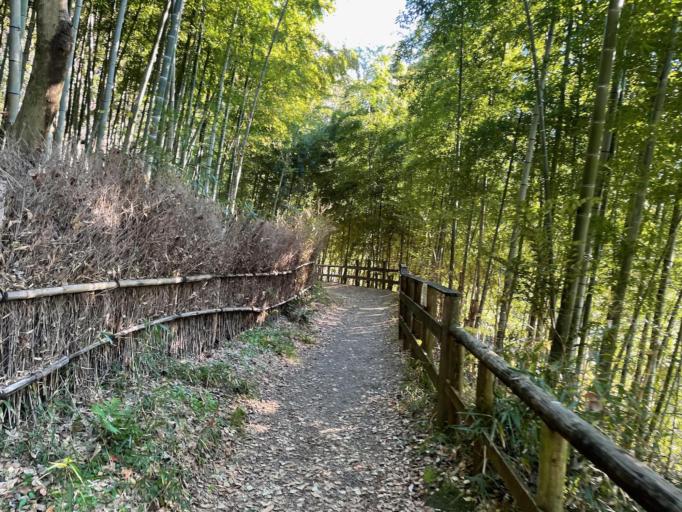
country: JP
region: Tokyo
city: Chofugaoka
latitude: 35.6184
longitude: 139.5247
